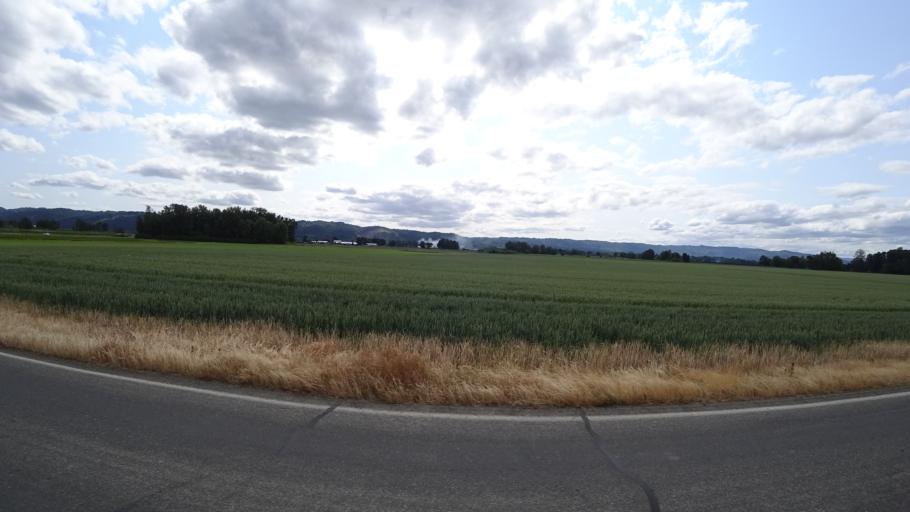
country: US
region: Washington
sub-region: Clark County
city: Felida
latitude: 45.6492
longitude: -122.7771
